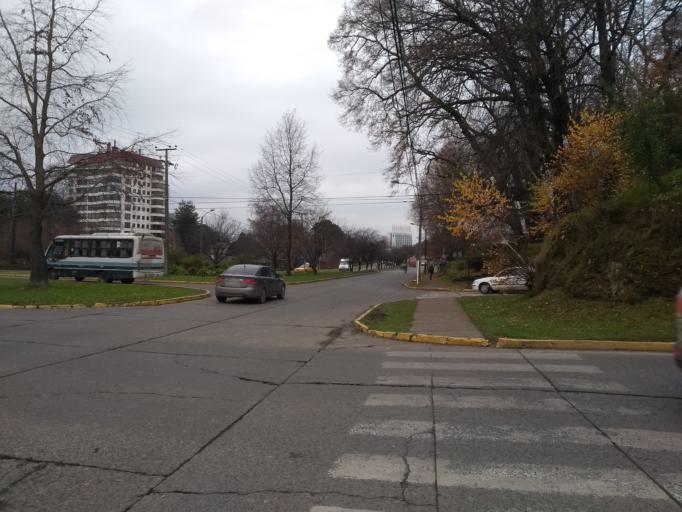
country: CL
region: Los Rios
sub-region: Provincia de Valdivia
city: Valdivia
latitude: -39.8098
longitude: -73.2578
